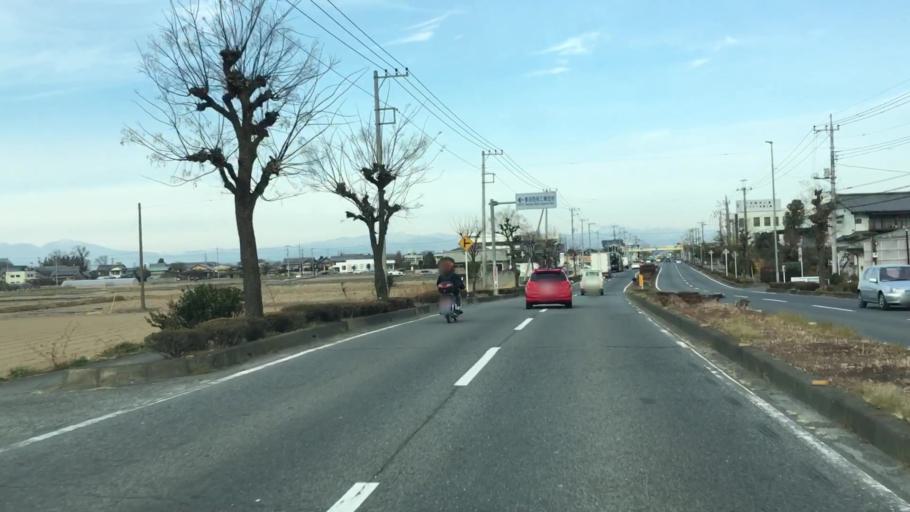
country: JP
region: Saitama
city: Menuma
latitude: 36.2198
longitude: 139.3682
